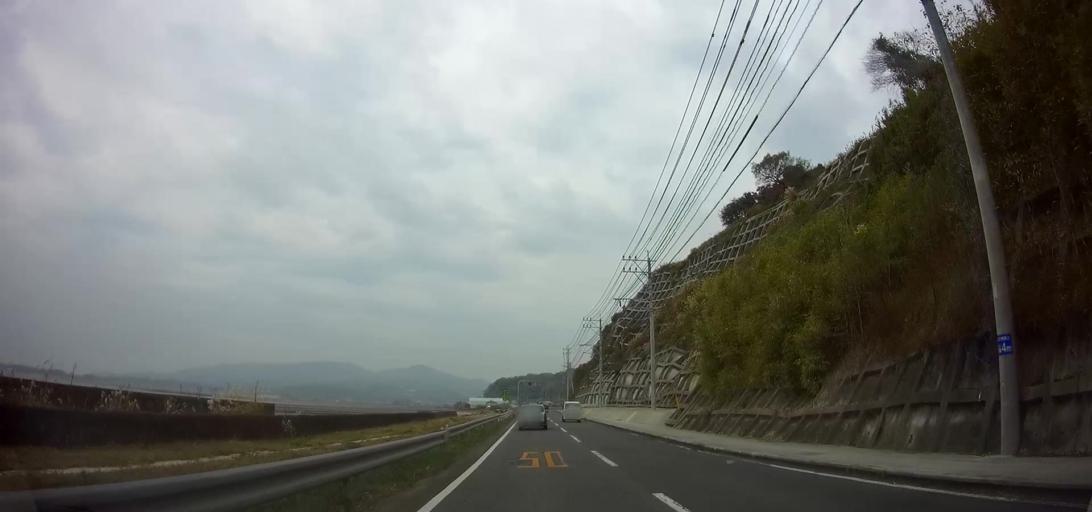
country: JP
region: Nagasaki
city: Shimabara
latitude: 32.6541
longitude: 130.2758
